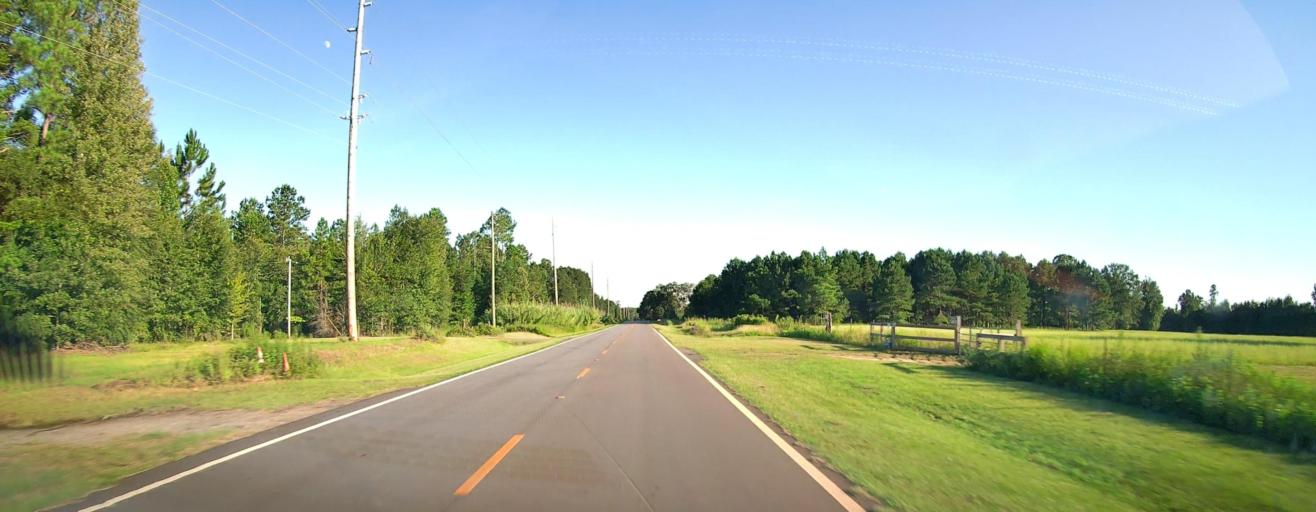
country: US
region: Georgia
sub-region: Pulaski County
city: Hawkinsville
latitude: 32.3107
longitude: -83.4522
